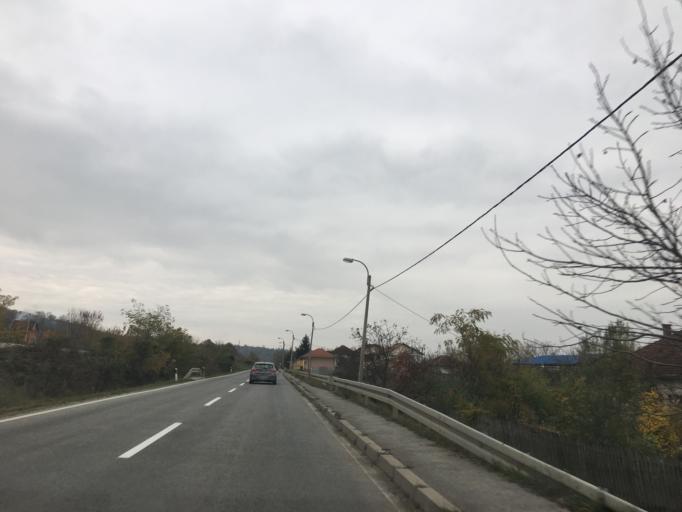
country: RS
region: Central Serbia
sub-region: Raski Okrug
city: Kraljevo
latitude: 43.7245
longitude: 20.7651
